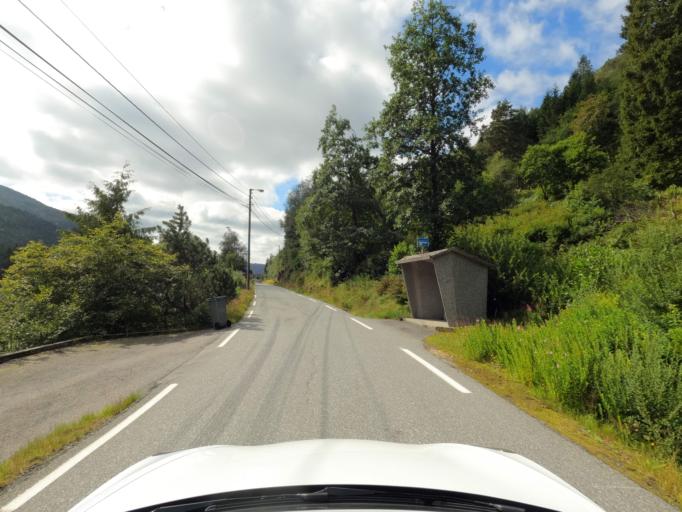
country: NO
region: Hordaland
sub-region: Os
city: Syfteland
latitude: 60.2811
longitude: 5.4613
